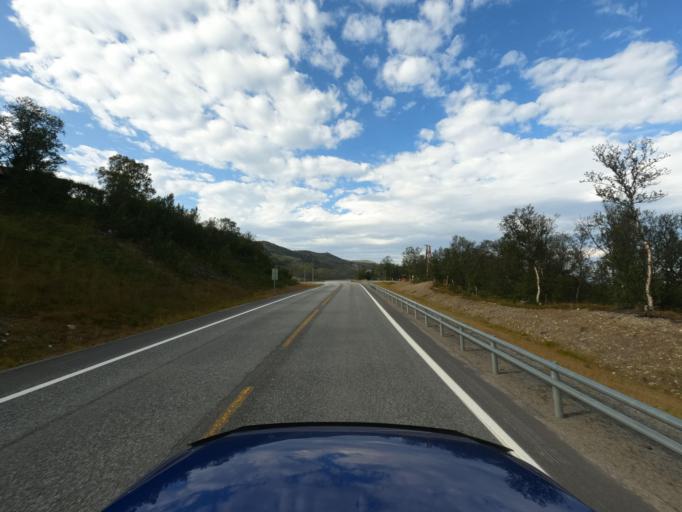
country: NO
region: Finnmark Fylke
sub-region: Kvalsund
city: Kvalsund
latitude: 70.4448
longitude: 24.3239
